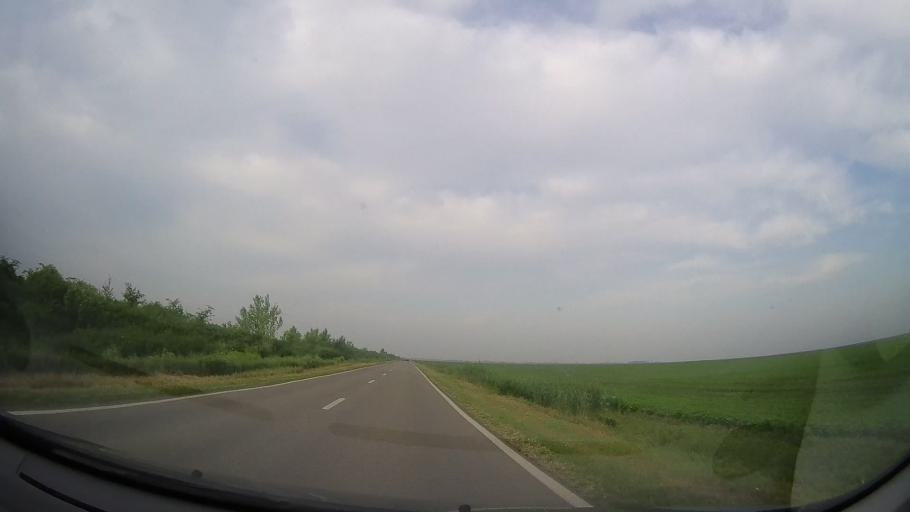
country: RO
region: Timis
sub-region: Comuna Peciu Nou
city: Peciu Nou
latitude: 45.6275
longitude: 21.0942
